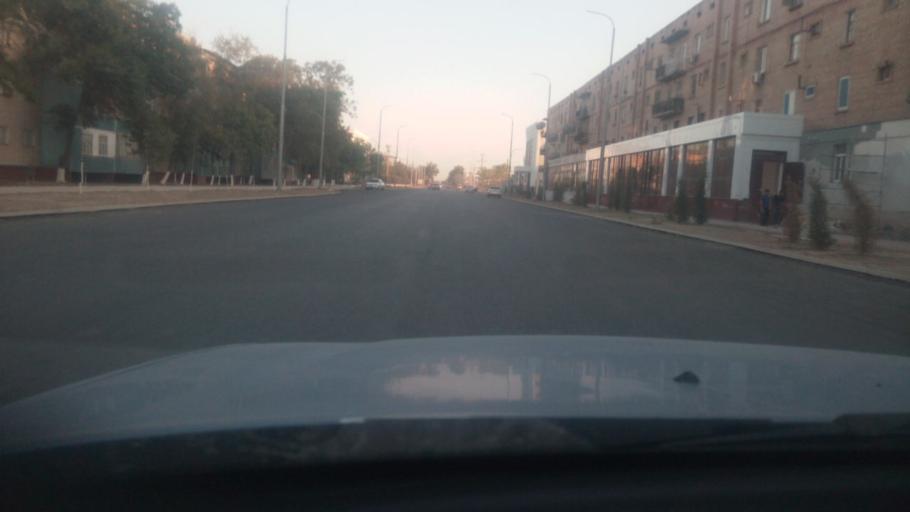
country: UZ
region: Sirdaryo
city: Guliston
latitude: 40.5027
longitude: 68.7751
